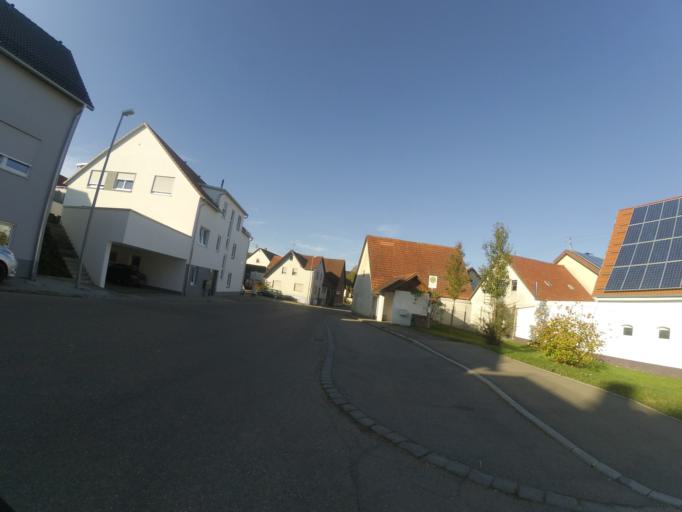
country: DE
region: Baden-Wuerttemberg
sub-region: Tuebingen Region
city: Blaubeuren
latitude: 48.4370
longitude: 9.8183
